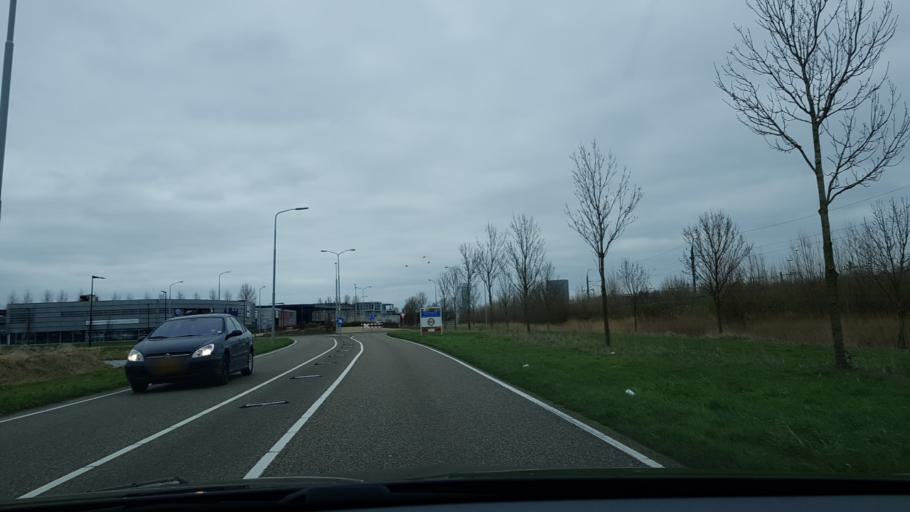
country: NL
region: North Holland
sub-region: Gemeente Haarlemmermeer
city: Hoofddorp
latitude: 52.2852
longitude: 4.6780
